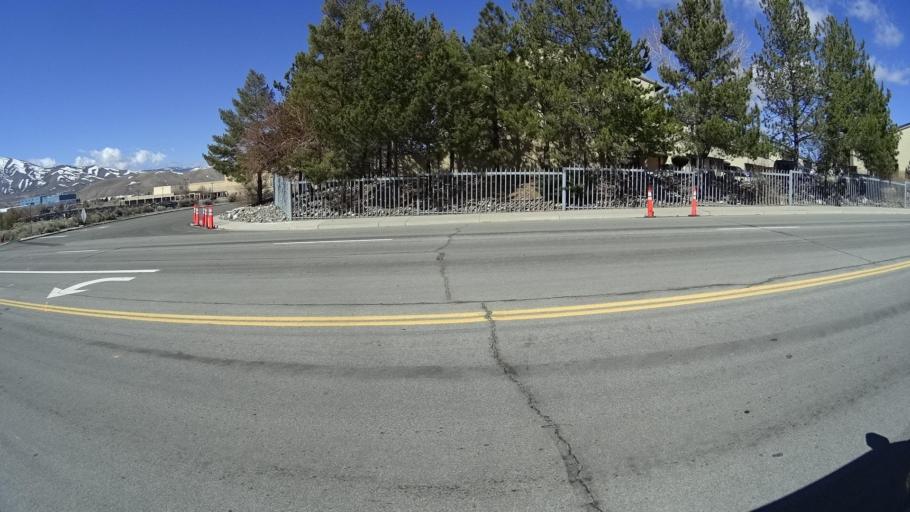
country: US
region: Nevada
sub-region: Washoe County
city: Lemmon Valley
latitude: 39.6448
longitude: -119.8812
